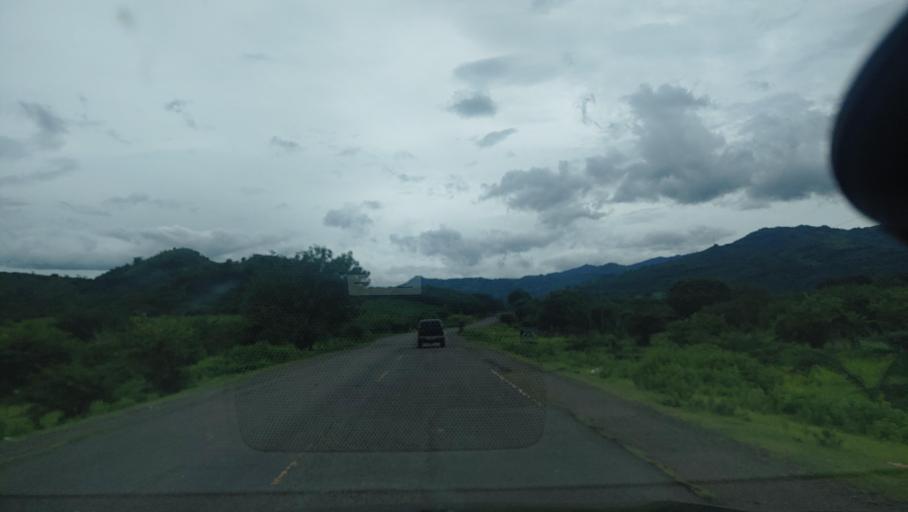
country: HN
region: Choluteca
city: Santa Ana de Yusguare
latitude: 13.3555
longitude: -87.1003
